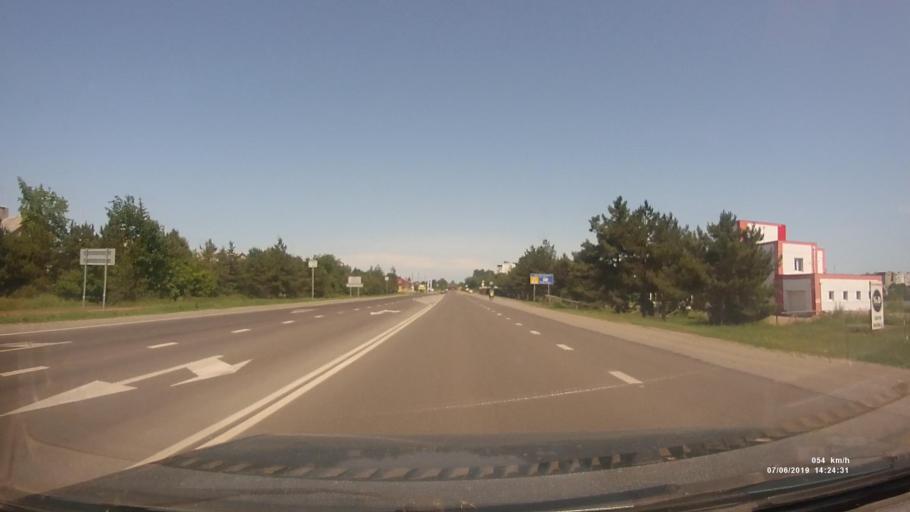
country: RU
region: Rostov
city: Kuleshovka
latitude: 47.0816
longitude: 39.5288
